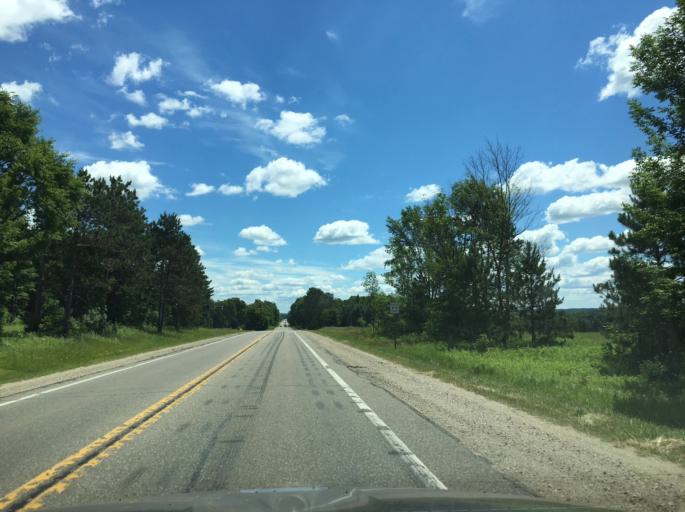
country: US
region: Michigan
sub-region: Osceola County
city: Reed City
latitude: 43.8725
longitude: -85.4365
